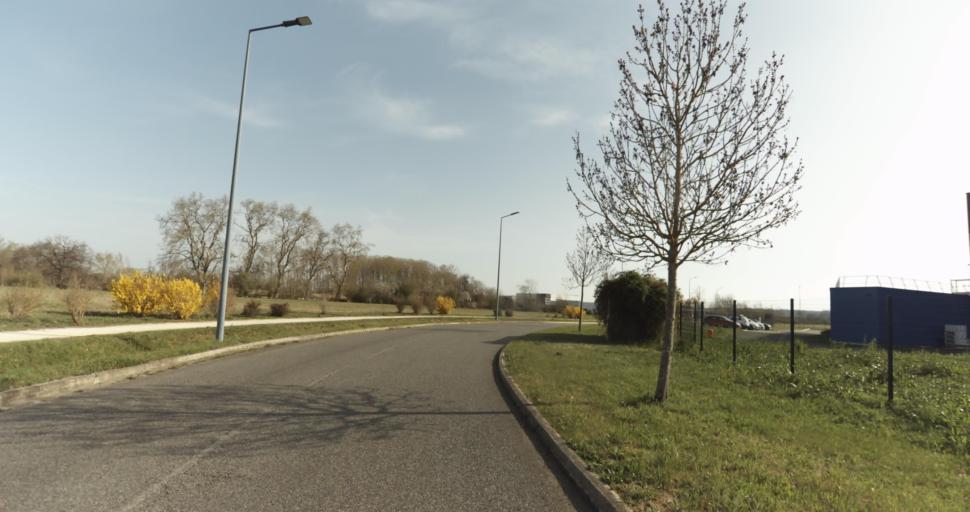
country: FR
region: Midi-Pyrenees
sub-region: Departement du Tarn
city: Saint-Sulpice-la-Pointe
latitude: 43.7648
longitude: 1.7116
